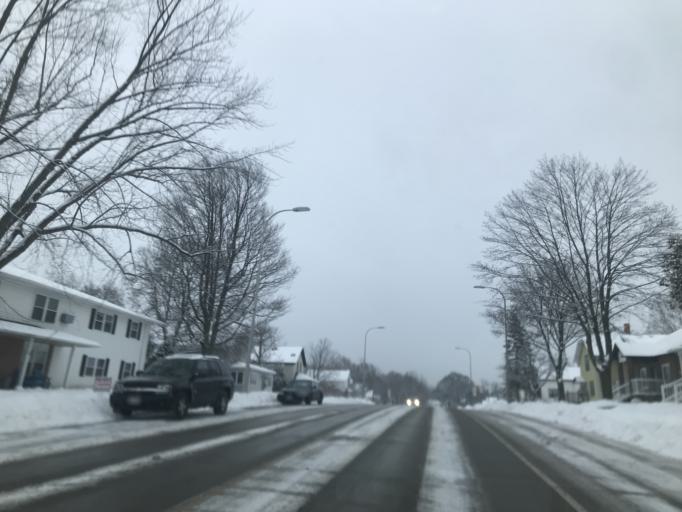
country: US
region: Wisconsin
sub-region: Oconto County
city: Oconto Falls
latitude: 44.8736
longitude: -88.1423
